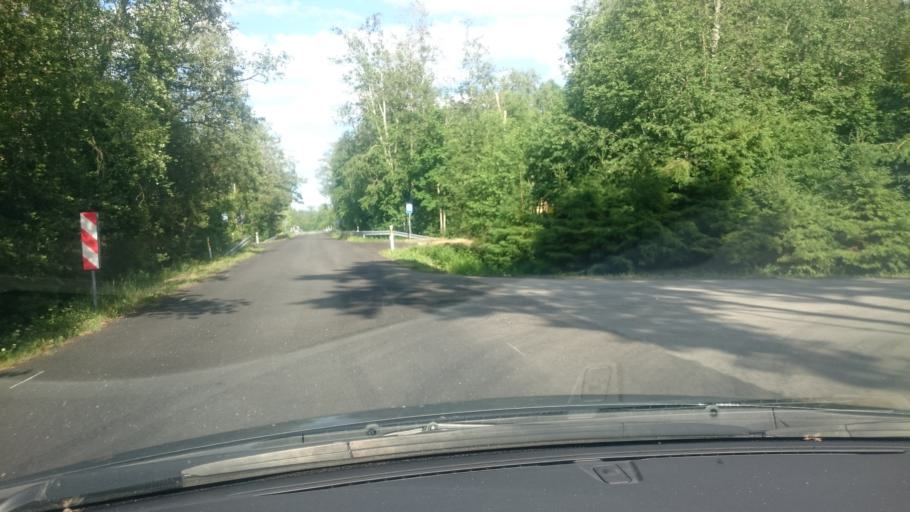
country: EE
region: Harju
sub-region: Rae vald
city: Vaida
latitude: 59.2270
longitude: 25.0002
